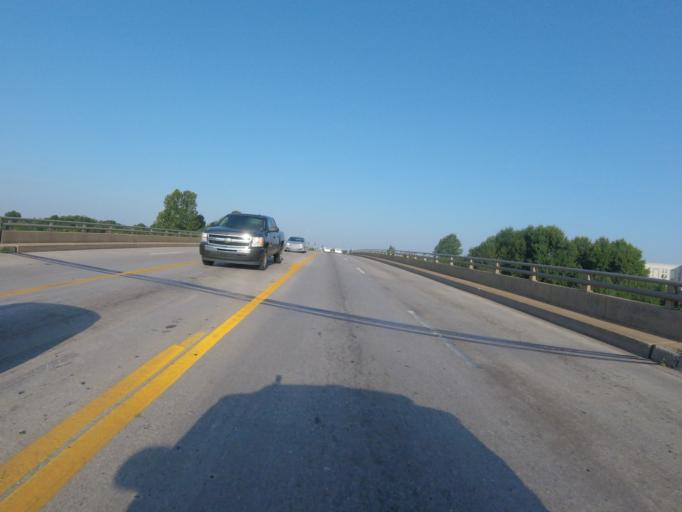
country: US
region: Arkansas
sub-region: Washington County
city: Fayetteville
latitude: 36.0783
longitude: -94.2001
